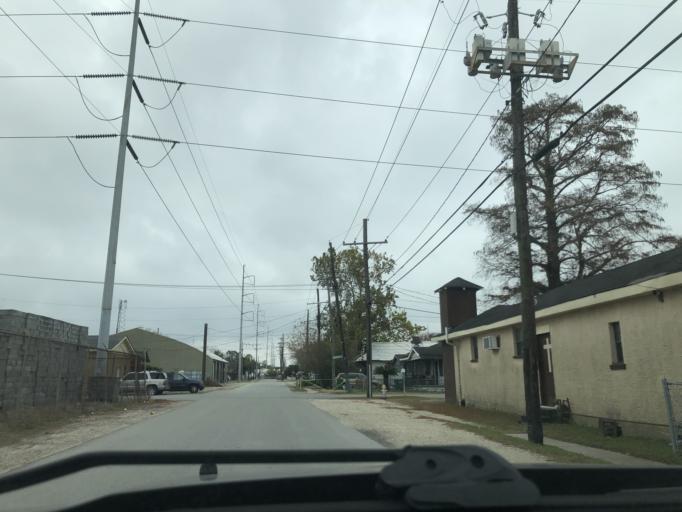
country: US
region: Louisiana
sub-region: Jefferson Parish
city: Metairie Terrace
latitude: 29.9727
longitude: -90.1624
